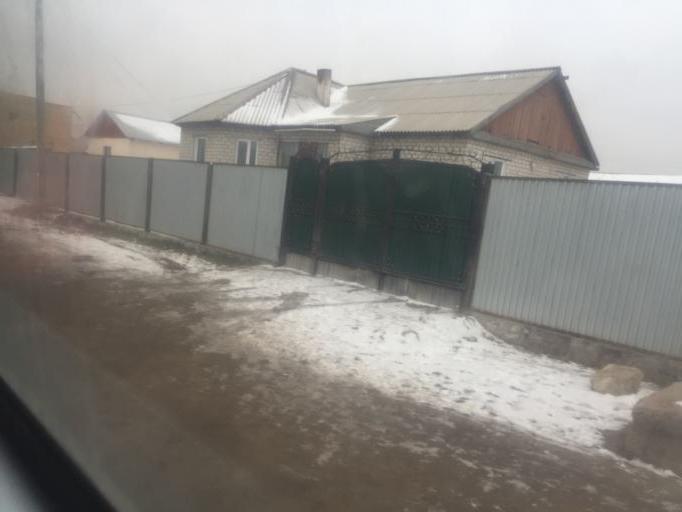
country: KZ
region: Astana Qalasy
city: Astana
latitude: 51.2039
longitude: 71.4126
